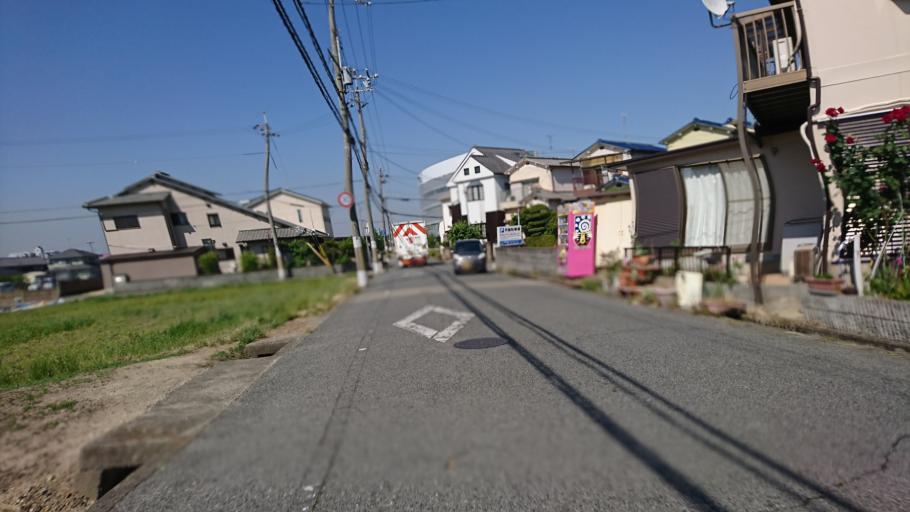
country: JP
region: Hyogo
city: Kakogawacho-honmachi
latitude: 34.7574
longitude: 134.8688
